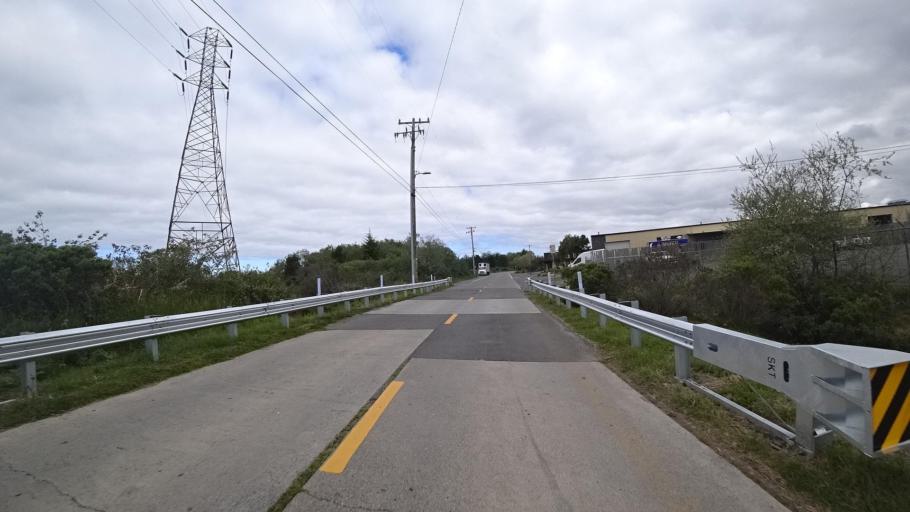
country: US
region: California
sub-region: Humboldt County
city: Arcata
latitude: 40.8561
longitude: -124.0894
